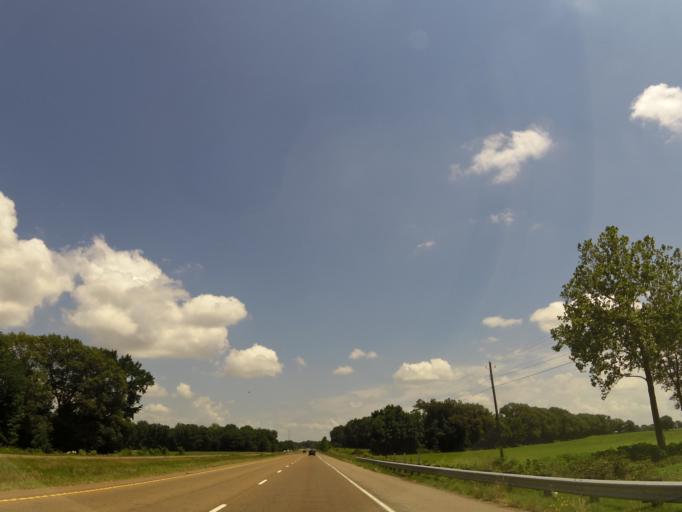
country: US
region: Tennessee
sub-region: Lauderdale County
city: Halls
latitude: 35.9289
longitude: -89.2851
